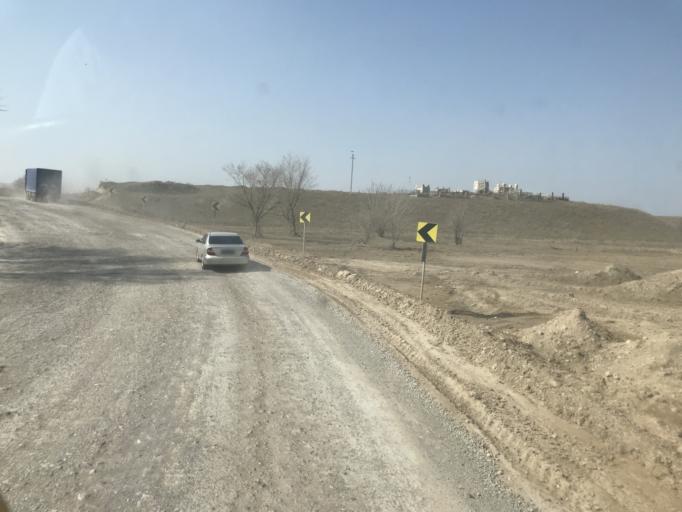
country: KG
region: Chuy
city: Bystrovka
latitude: 43.3209
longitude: 76.0037
